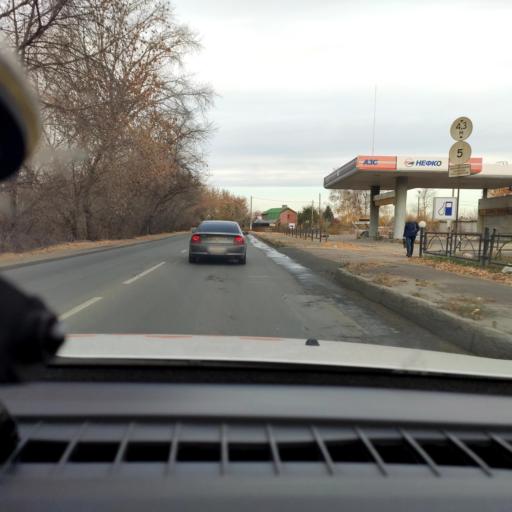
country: RU
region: Samara
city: Novokuybyshevsk
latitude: 53.1448
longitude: 50.0296
